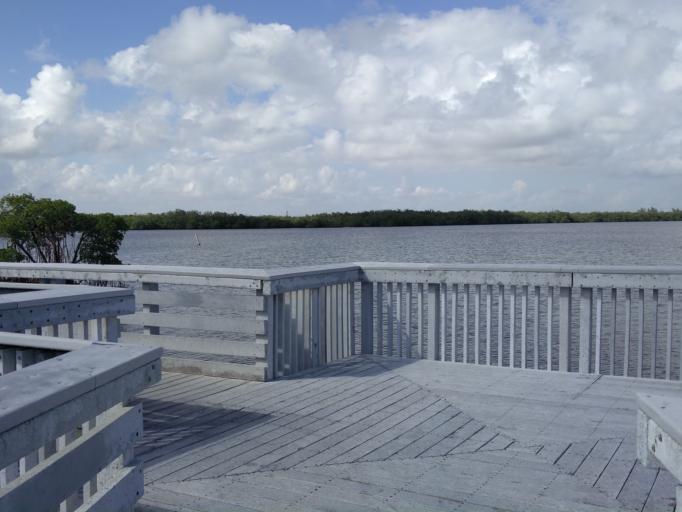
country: US
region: Florida
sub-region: Broward County
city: Dania Beach
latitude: 26.0398
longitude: -80.1216
